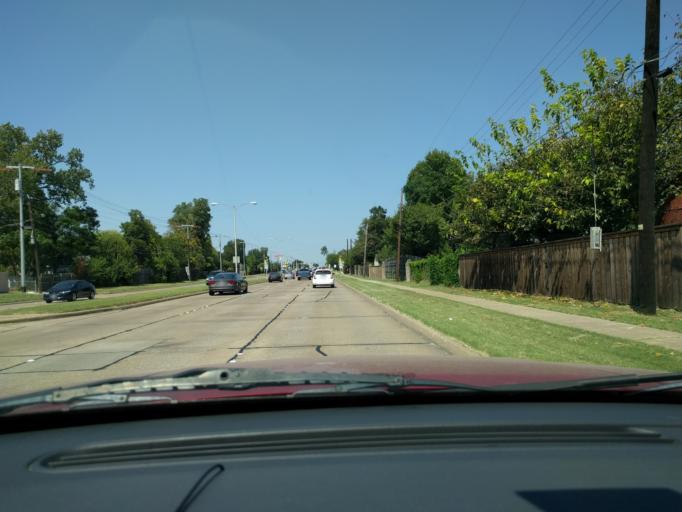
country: US
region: Texas
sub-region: Dallas County
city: Richardson
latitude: 32.9265
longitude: -96.7000
